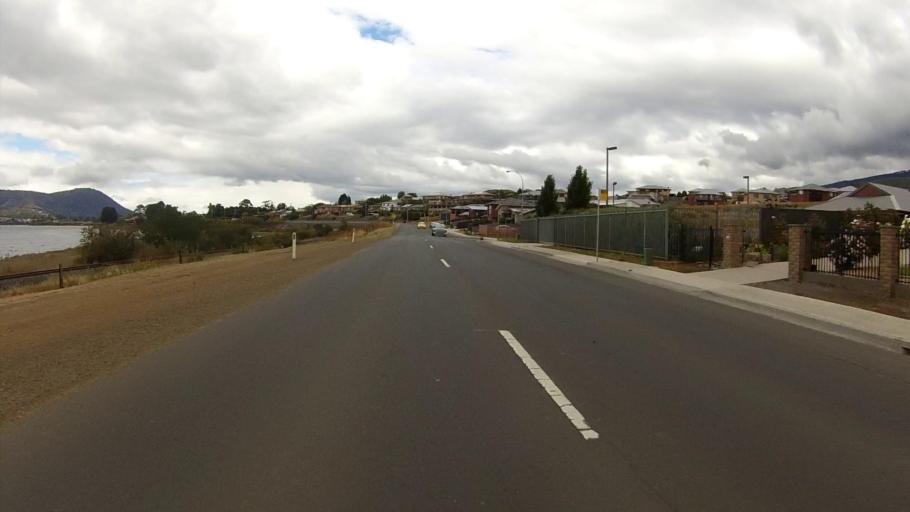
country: AU
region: Tasmania
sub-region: Glenorchy
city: Granton
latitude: -42.7573
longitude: 147.2359
